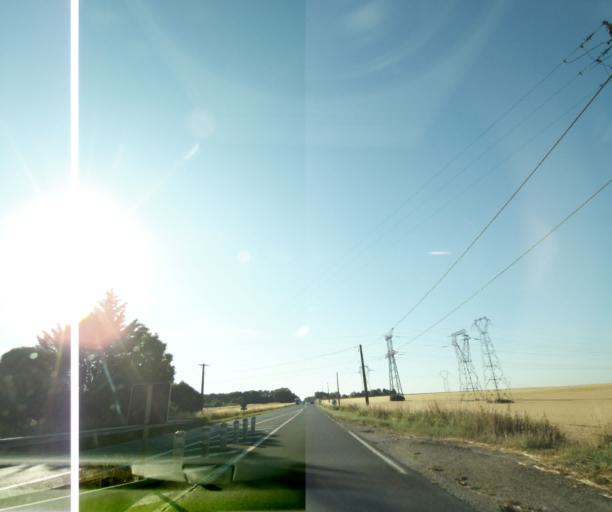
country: FR
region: Ile-de-France
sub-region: Departement de Seine-et-Marne
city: Vernou-la-Celle-sur-Seine
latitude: 48.3636
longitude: 2.8563
